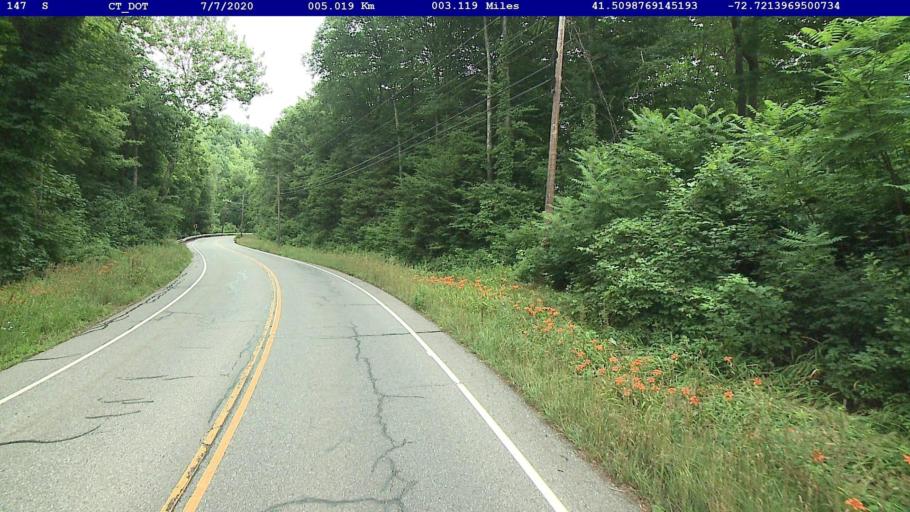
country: US
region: Connecticut
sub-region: Middlesex County
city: Durham
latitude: 41.5098
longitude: -72.7213
